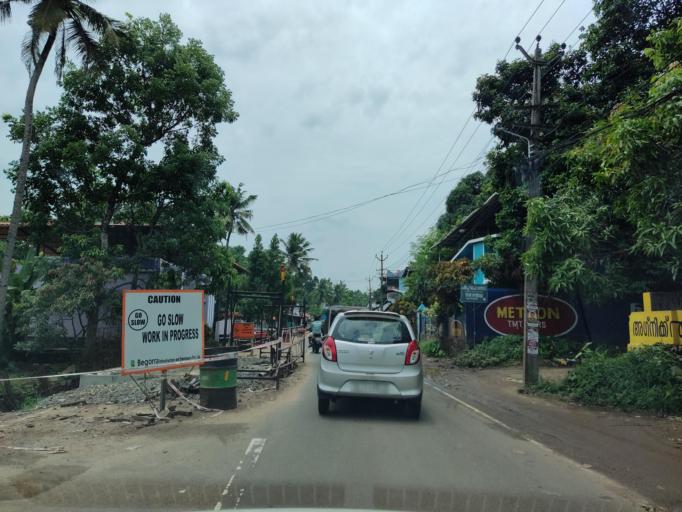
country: IN
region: Kerala
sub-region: Pattanamtitta
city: Adur
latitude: 9.2284
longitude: 76.6645
